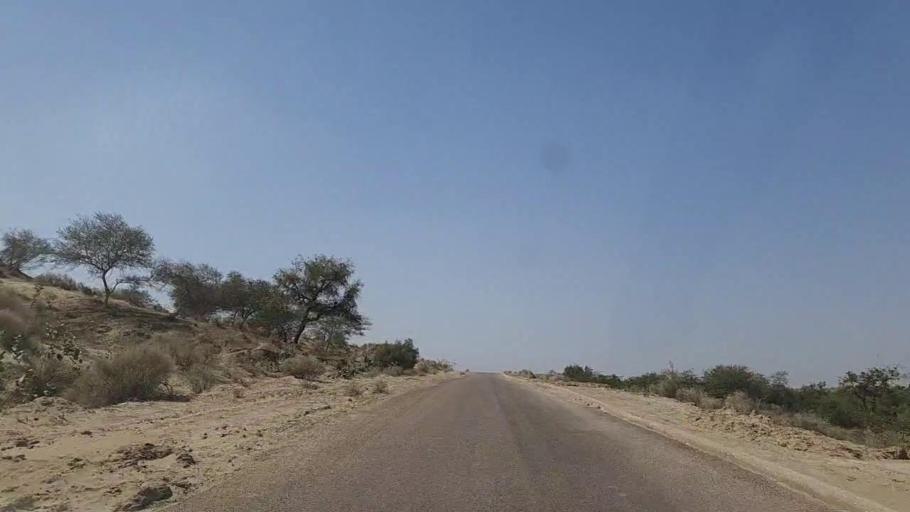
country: PK
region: Sindh
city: Diplo
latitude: 24.5497
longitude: 69.4275
